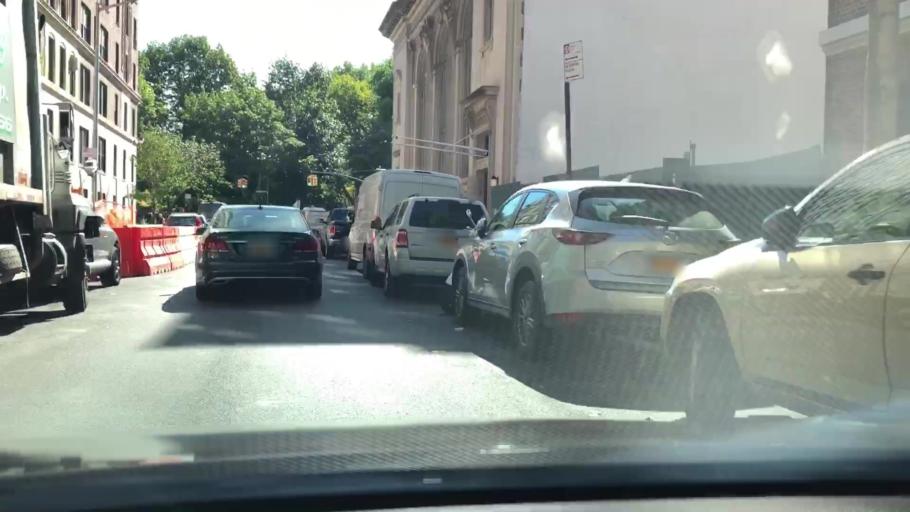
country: US
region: New York
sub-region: New York County
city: Manhattan
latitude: 40.7753
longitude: -73.9777
